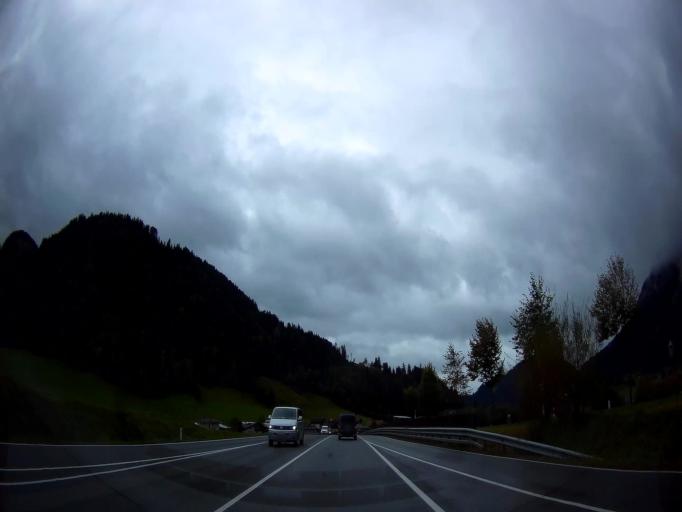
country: AT
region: Tyrol
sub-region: Politischer Bezirk Kufstein
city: Soll
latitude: 47.5010
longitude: 12.1914
